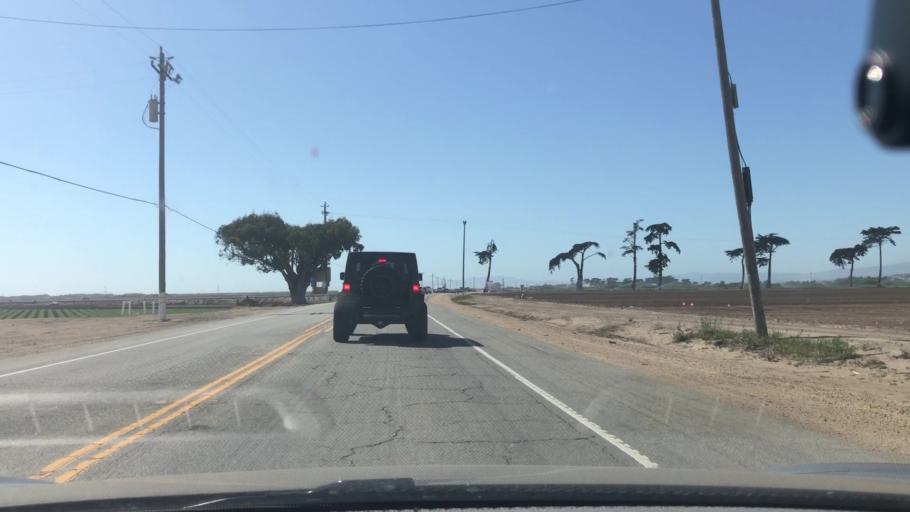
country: US
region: California
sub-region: Monterey County
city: Castroville
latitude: 36.7757
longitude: -121.7720
